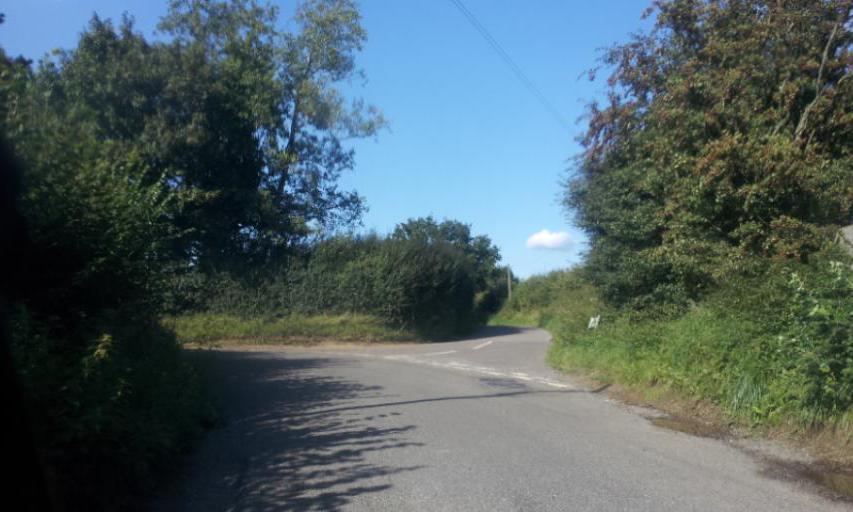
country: GB
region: England
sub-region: Kent
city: East Peckham
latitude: 51.2184
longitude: 0.3654
